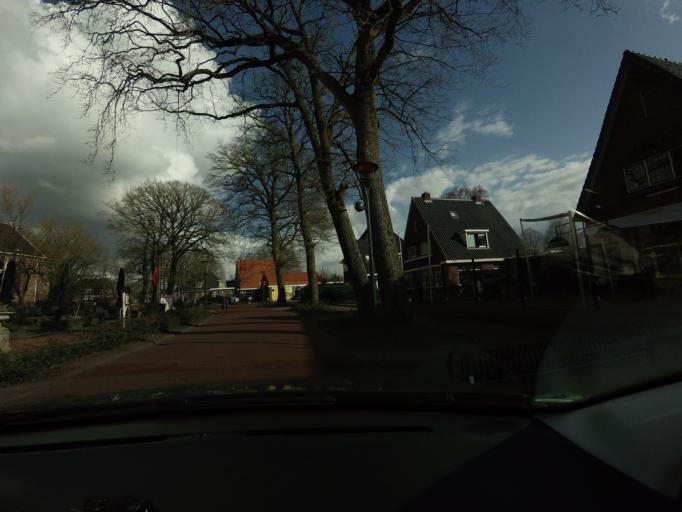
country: NL
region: Drenthe
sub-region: Gemeente Assen
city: Assen
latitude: 52.8500
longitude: 6.6086
